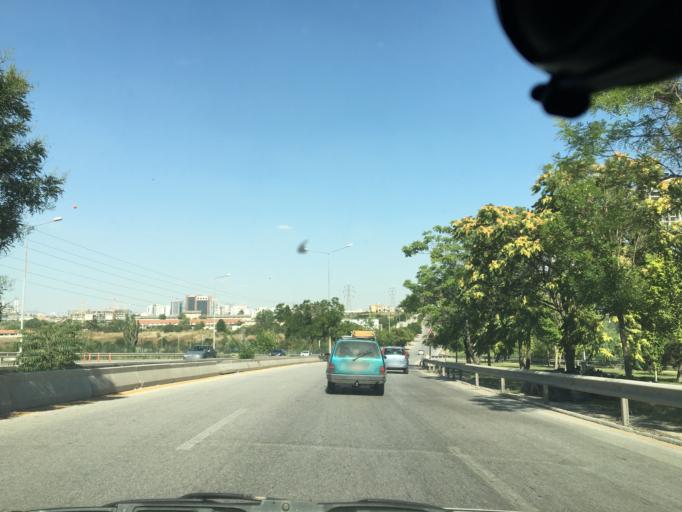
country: TR
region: Ankara
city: Batikent
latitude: 39.9186
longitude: 32.7820
